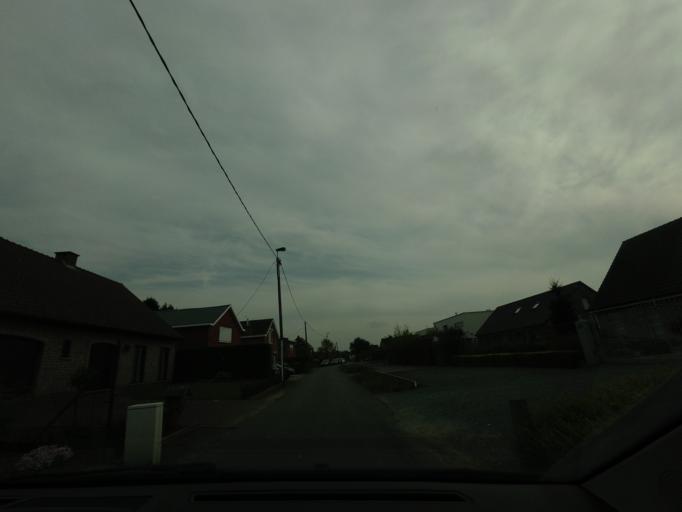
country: BE
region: Flanders
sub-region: Provincie Antwerpen
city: Rumst
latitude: 51.0857
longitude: 4.4644
